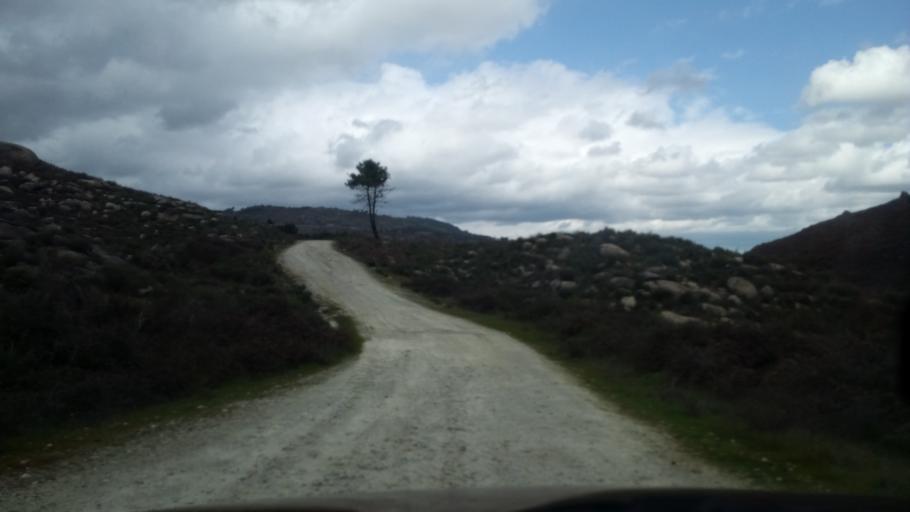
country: PT
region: Guarda
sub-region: Fornos de Algodres
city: Fornos de Algodres
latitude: 40.5889
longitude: -7.5676
